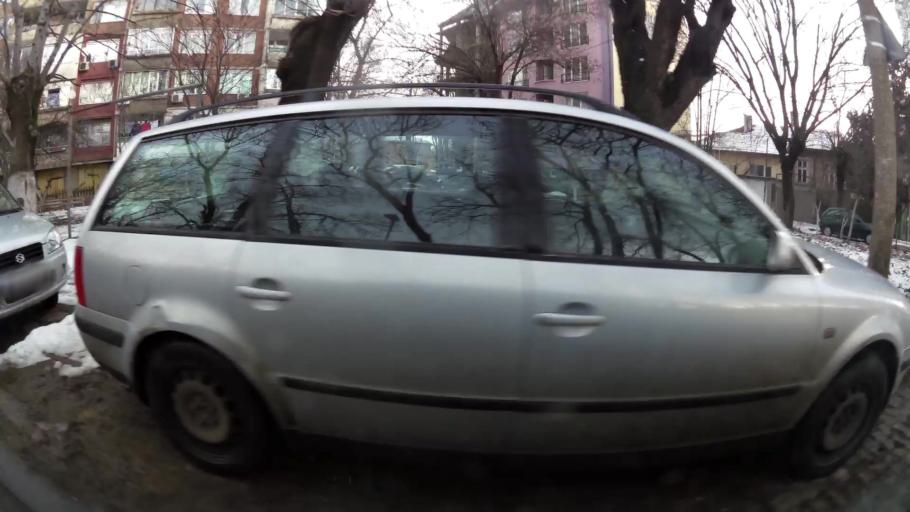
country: BG
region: Sofia-Capital
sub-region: Stolichna Obshtina
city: Sofia
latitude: 42.6987
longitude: 23.2944
